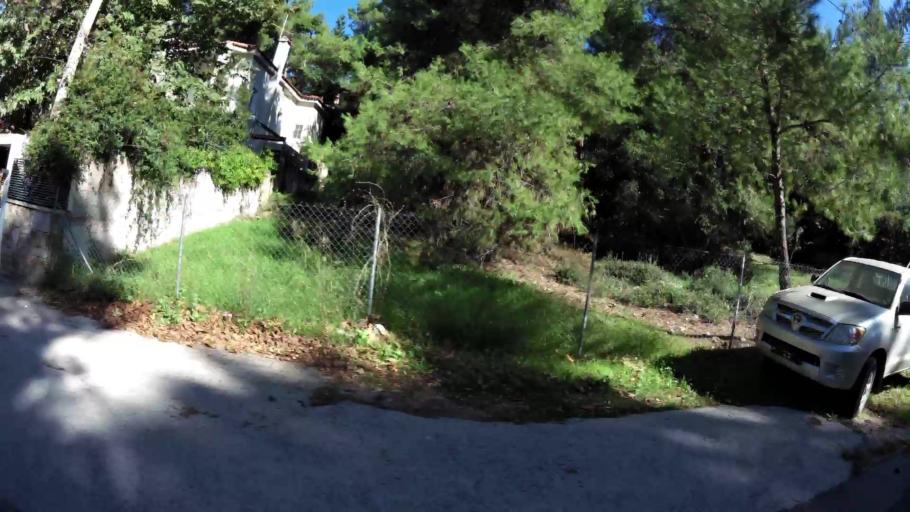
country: GR
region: Attica
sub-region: Nomarchia Anatolikis Attikis
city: Rodopoli
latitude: 38.1109
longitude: 23.8790
